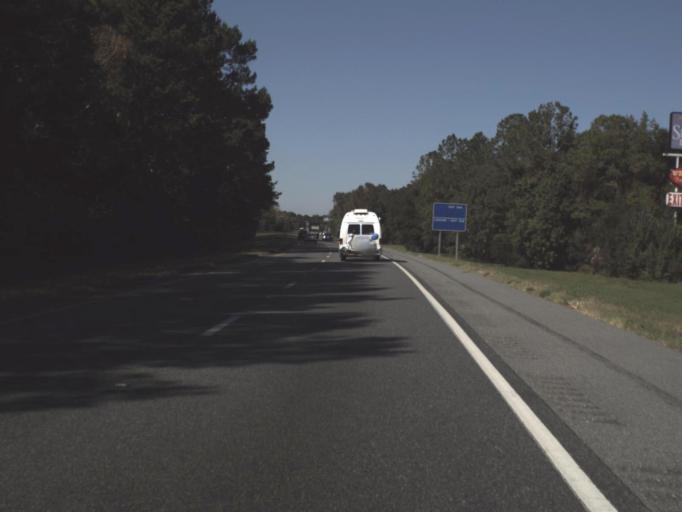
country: US
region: Florida
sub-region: Sumter County
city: Wildwood
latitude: 28.8326
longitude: -82.0363
